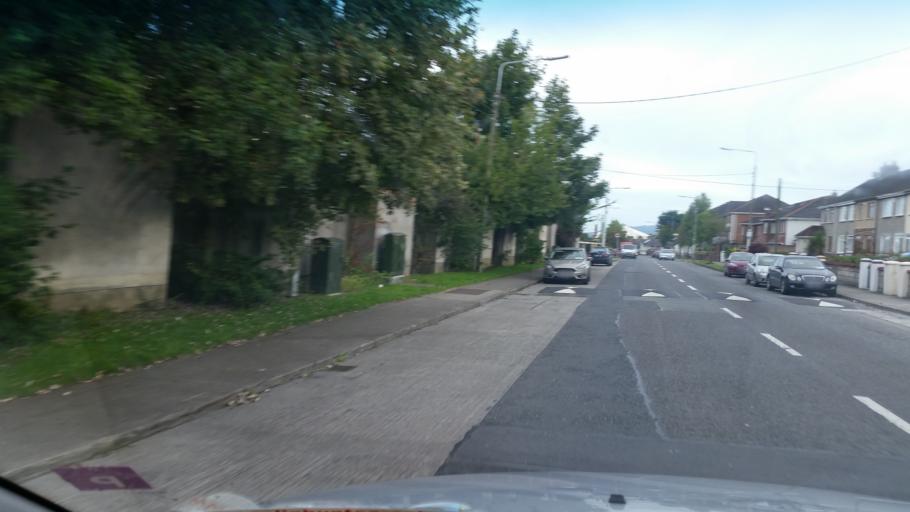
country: IE
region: Leinster
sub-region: Dublin City
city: Finglas
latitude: 53.3943
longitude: -6.3011
